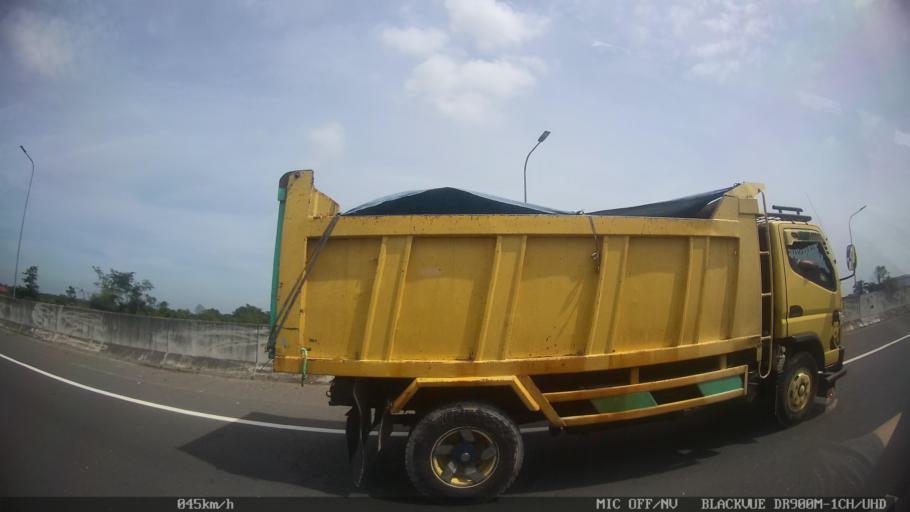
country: ID
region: North Sumatra
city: Medan
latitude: 3.6484
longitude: 98.6551
